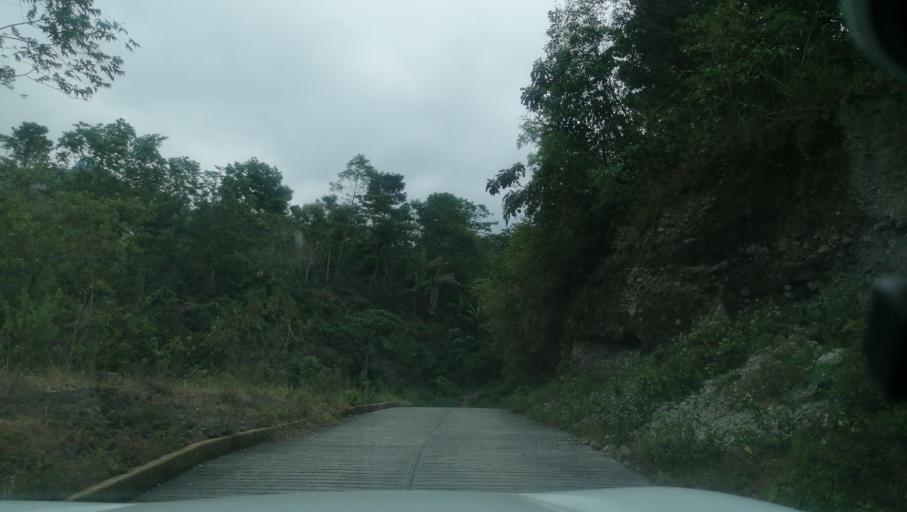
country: GT
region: San Marcos
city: Sibinal
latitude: 15.1662
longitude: -92.1615
